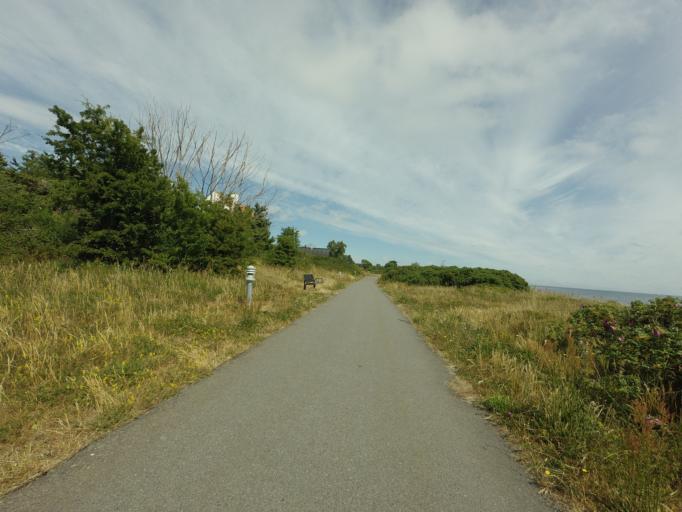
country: SE
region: Skane
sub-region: Simrishamns Kommun
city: Simrishamn
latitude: 55.5222
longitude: 14.3474
